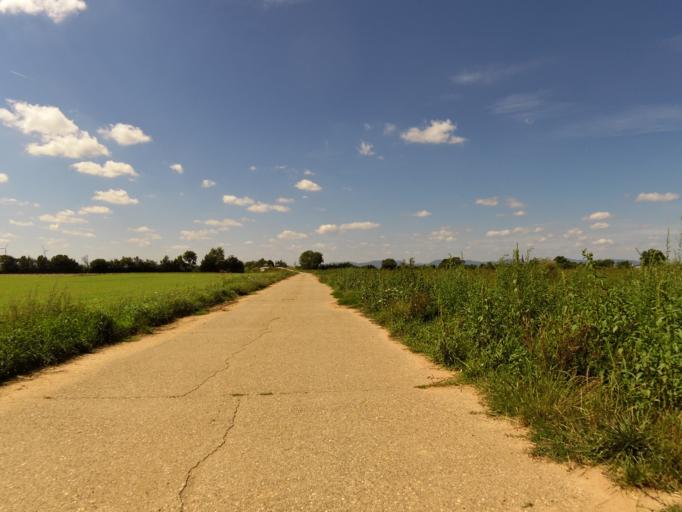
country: DE
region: Rheinland-Pfalz
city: Rulzheim
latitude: 49.1818
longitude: 8.2984
